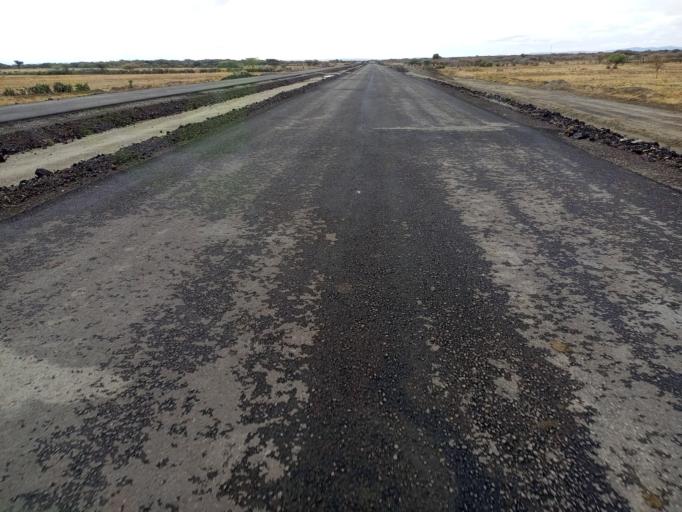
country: ET
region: Oromiya
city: Ziway
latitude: 7.6255
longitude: 38.6799
